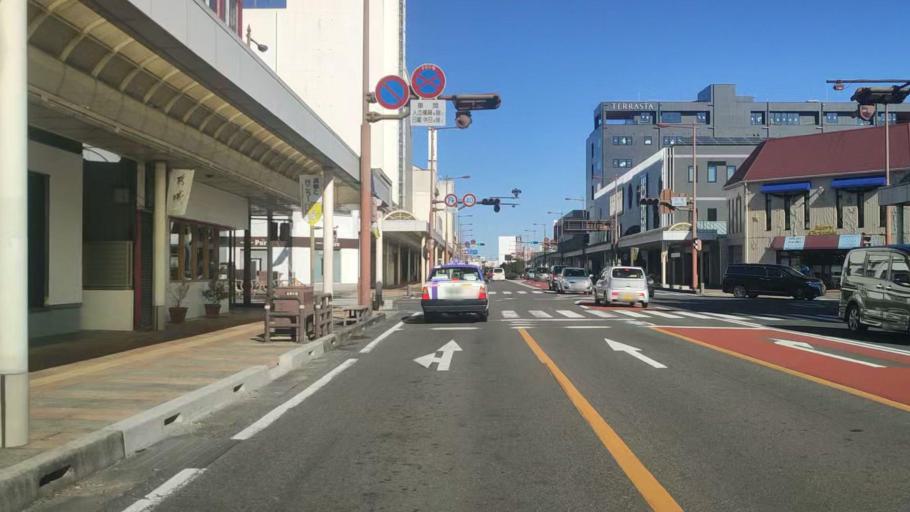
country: JP
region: Miyazaki
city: Miyakonojo
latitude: 31.7250
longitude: 131.0637
